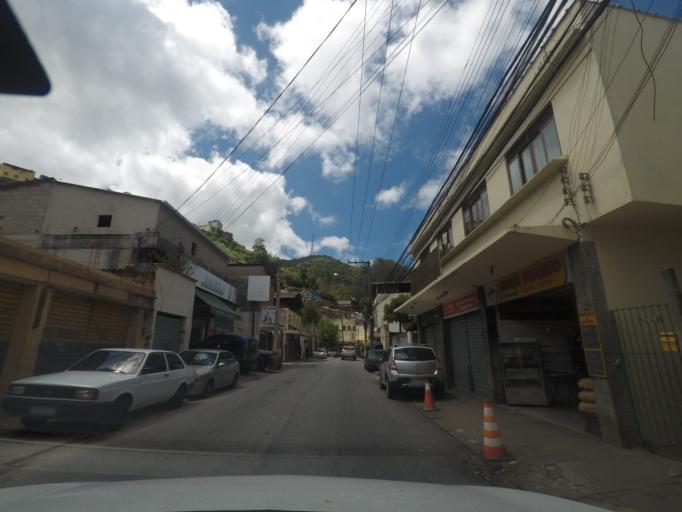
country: BR
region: Rio de Janeiro
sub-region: Teresopolis
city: Teresopolis
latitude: -22.4029
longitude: -42.9767
